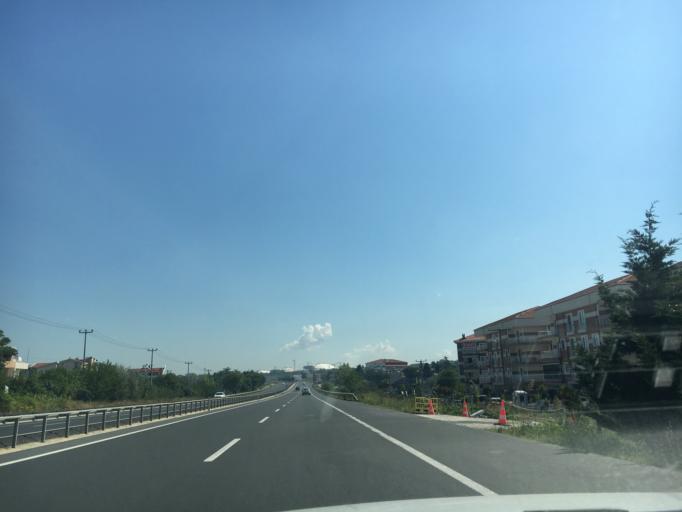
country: TR
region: Tekirdag
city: Marmara Ereglisi
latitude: 40.9837
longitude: 27.9648
